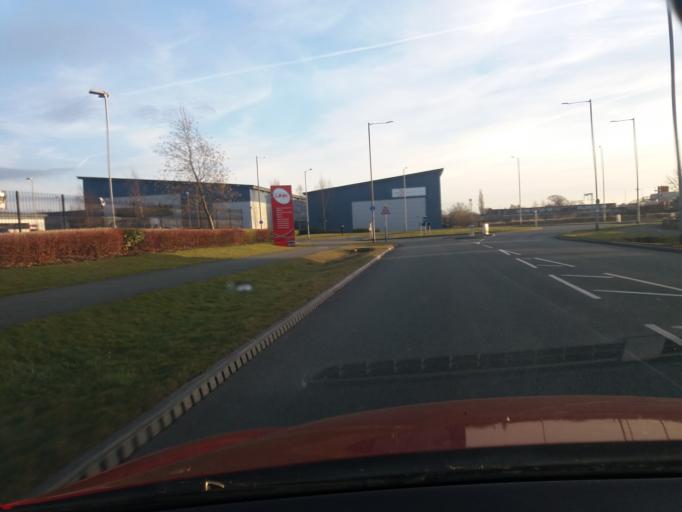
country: GB
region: England
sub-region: Lancashire
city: Euxton
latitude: 53.6747
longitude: -2.6566
